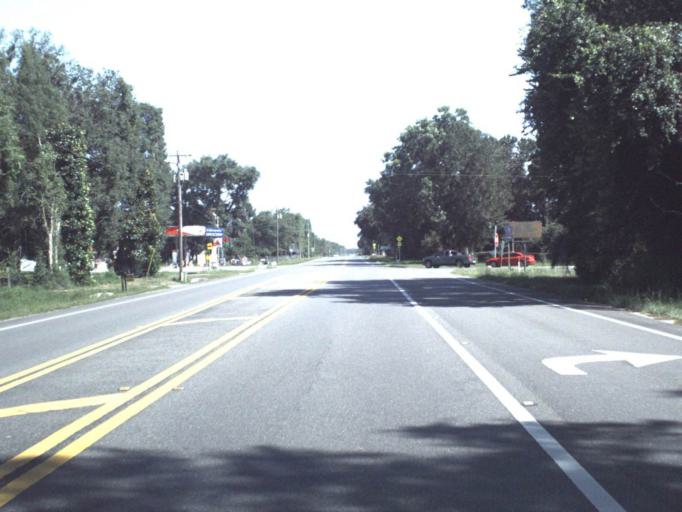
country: US
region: Florida
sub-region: Clay County
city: Keystone Heights
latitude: 29.8431
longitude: -82.0666
